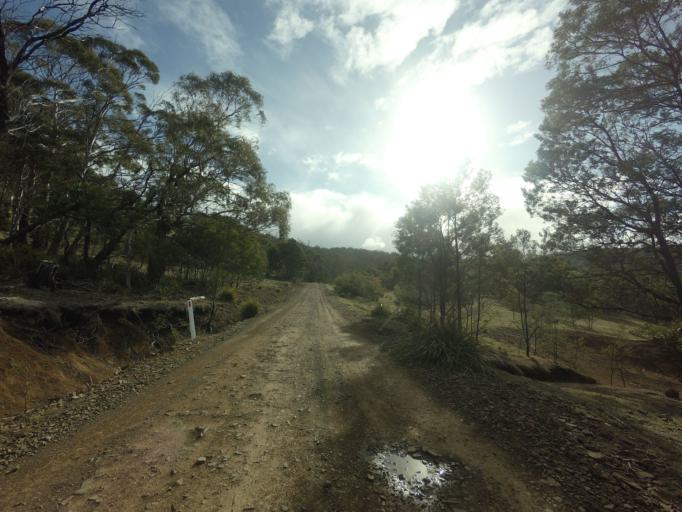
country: AU
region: Tasmania
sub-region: Sorell
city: Sorell
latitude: -42.2292
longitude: 148.0073
